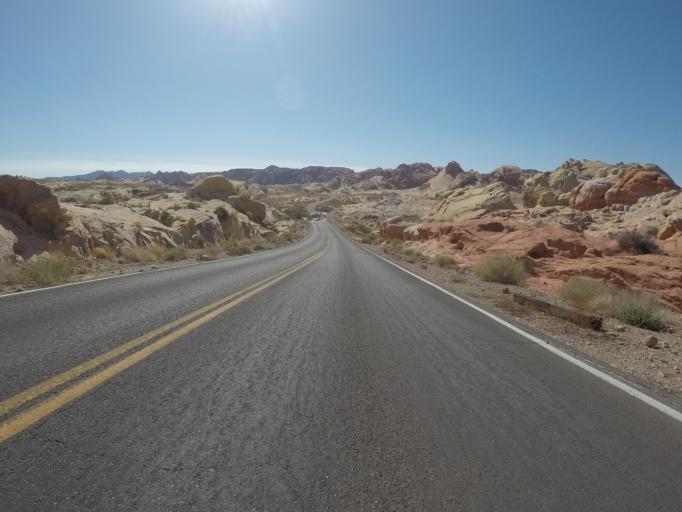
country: US
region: Nevada
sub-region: Clark County
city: Moapa Valley
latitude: 36.4814
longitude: -114.5261
